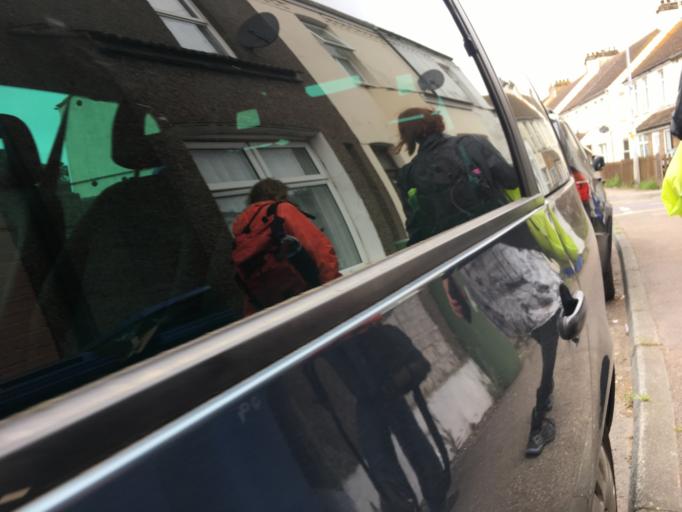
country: GB
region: England
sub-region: Kent
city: Queenborough
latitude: 51.4171
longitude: 0.7471
